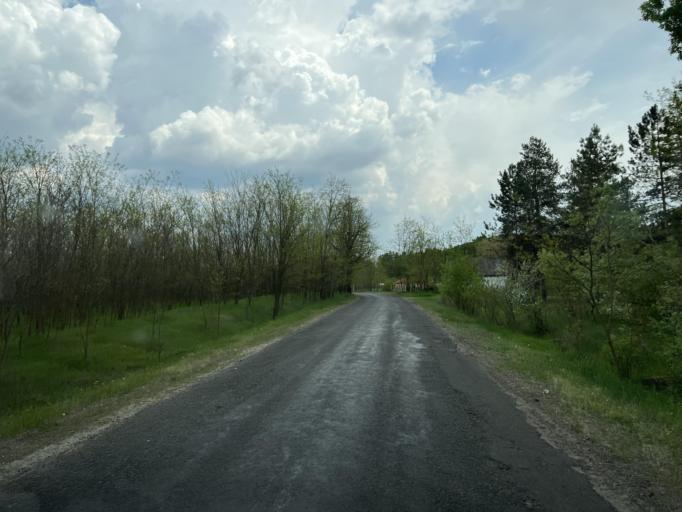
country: HU
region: Pest
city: Csemo
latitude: 47.1022
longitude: 19.7282
